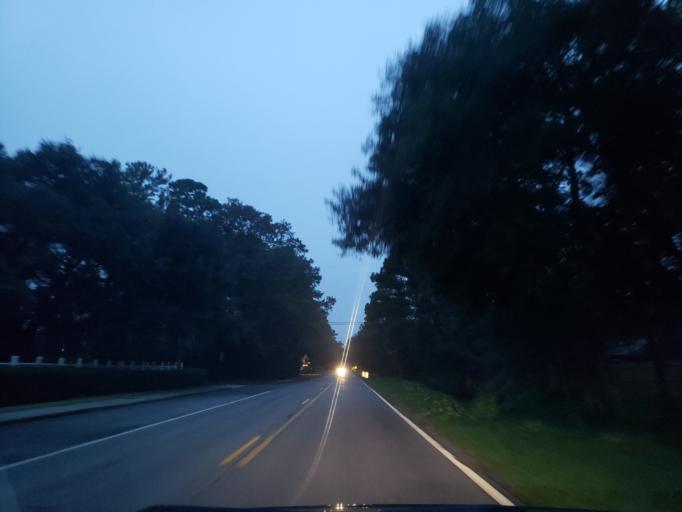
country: US
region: Georgia
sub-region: Chatham County
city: Wilmington Island
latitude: 32.0207
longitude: -80.9638
